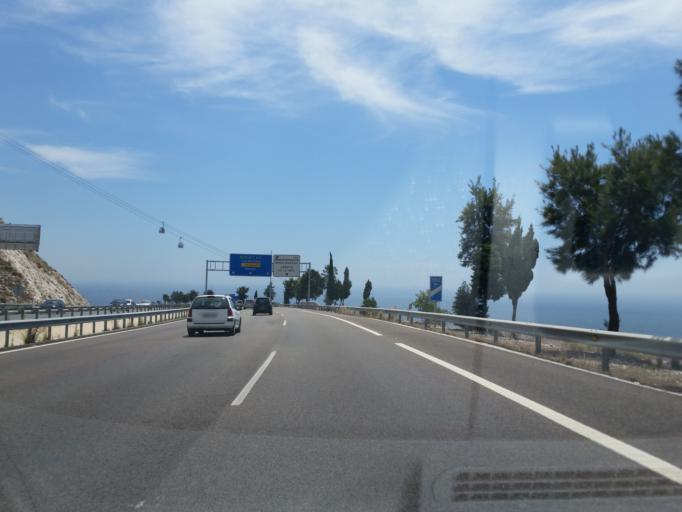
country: ES
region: Andalusia
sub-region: Provincia de Malaga
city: Benalmadena
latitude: 36.6057
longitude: -4.5504
